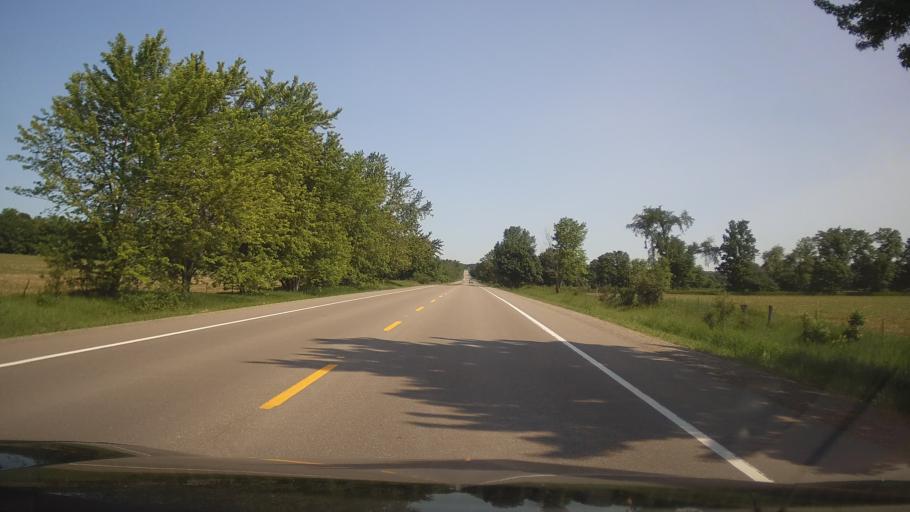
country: CA
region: Ontario
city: Omemee
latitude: 44.3702
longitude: -78.8963
